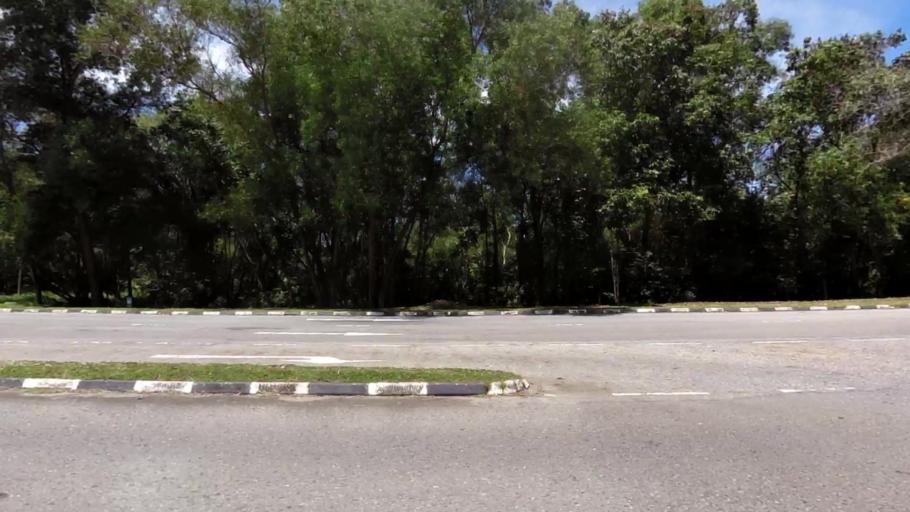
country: BN
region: Brunei and Muara
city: Bandar Seri Begawan
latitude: 4.9317
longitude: 114.9489
